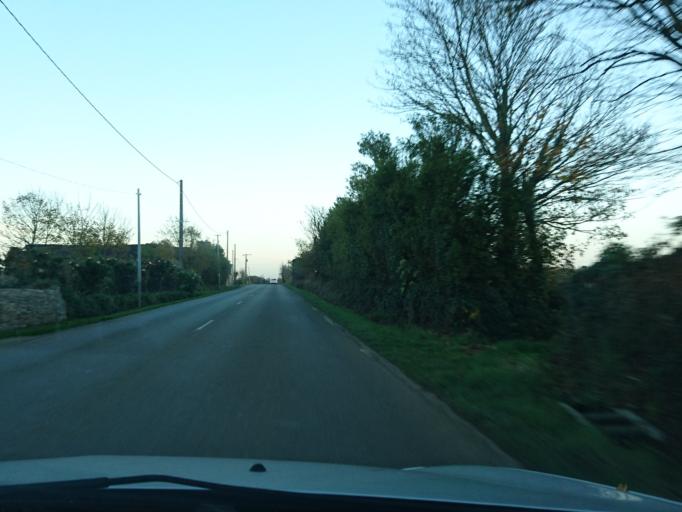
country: FR
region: Brittany
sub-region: Departement du Finistere
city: Lanrivoare
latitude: 48.4611
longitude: -4.6333
